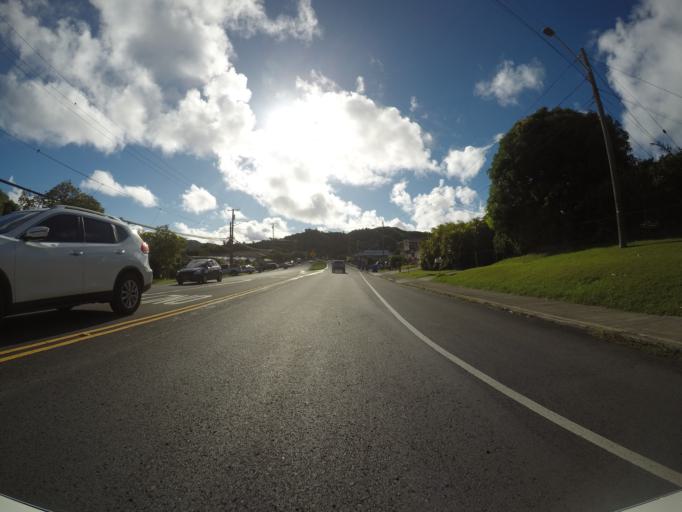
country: US
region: Hawaii
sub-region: Honolulu County
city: Kane'ohe
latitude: 21.4109
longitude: -157.7762
